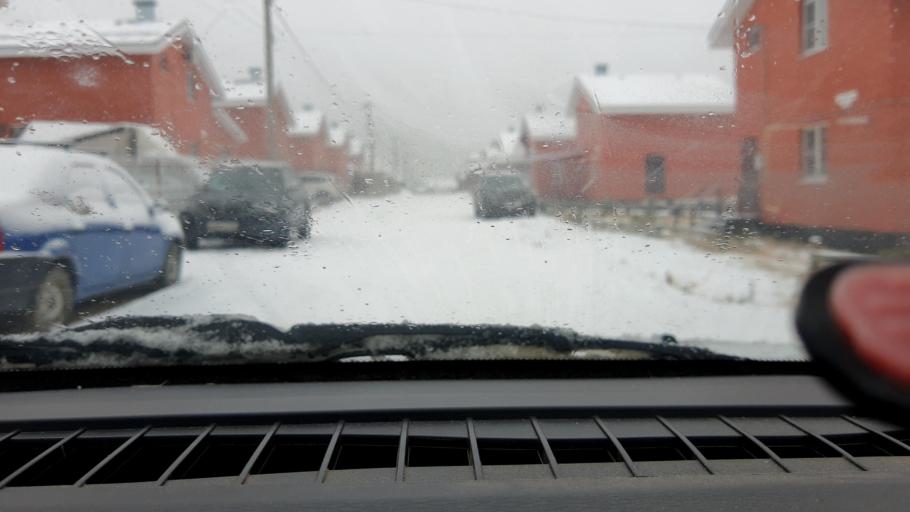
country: RU
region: Nizjnij Novgorod
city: Afonino
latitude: 56.1948
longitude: 44.0878
